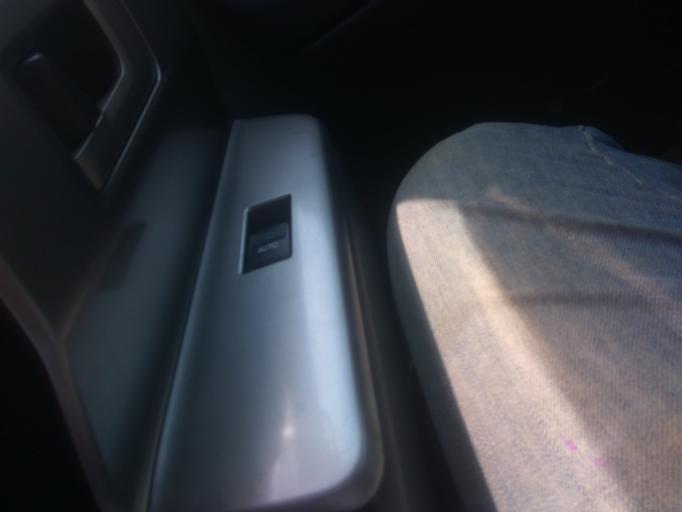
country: IN
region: Assam
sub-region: Karimganj
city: Karimganj
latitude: 24.8119
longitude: 92.1797
